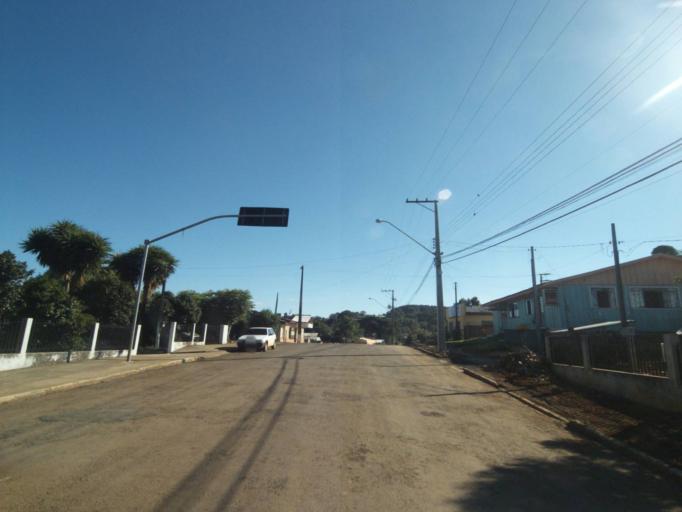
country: BR
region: Parana
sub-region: Pinhao
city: Pinhao
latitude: -25.8390
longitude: -52.0272
